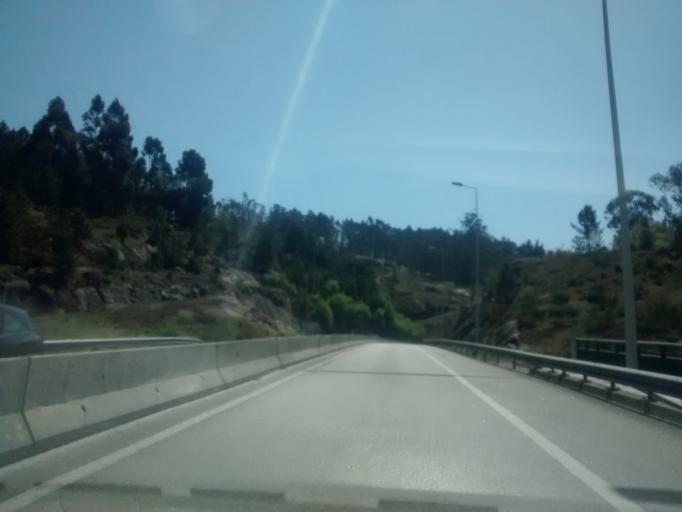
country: PT
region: Braga
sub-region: Braga
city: Braga
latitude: 41.5192
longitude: -8.4430
